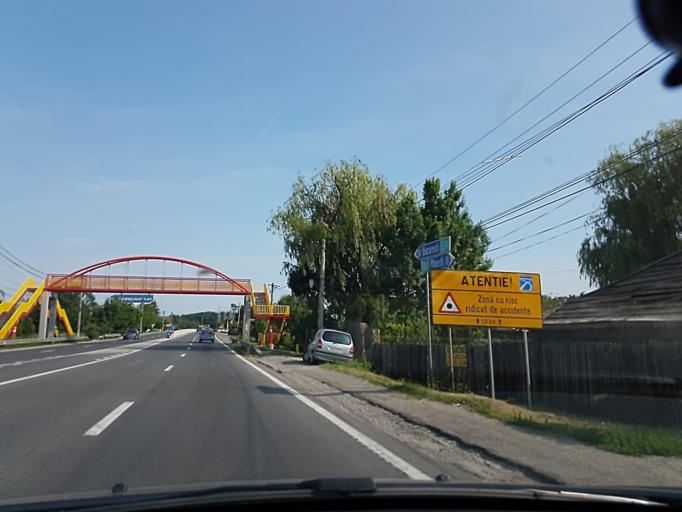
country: RO
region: Prahova
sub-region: Comuna Puchenii Mari
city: Pietrosani
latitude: 44.8533
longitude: 26.0751
